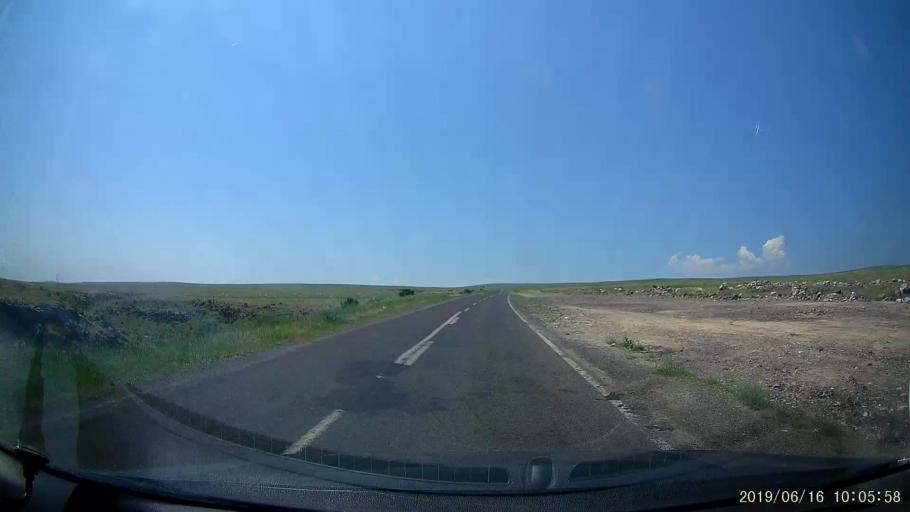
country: TR
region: Kars
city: Digor
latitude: 40.2623
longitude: 43.5403
